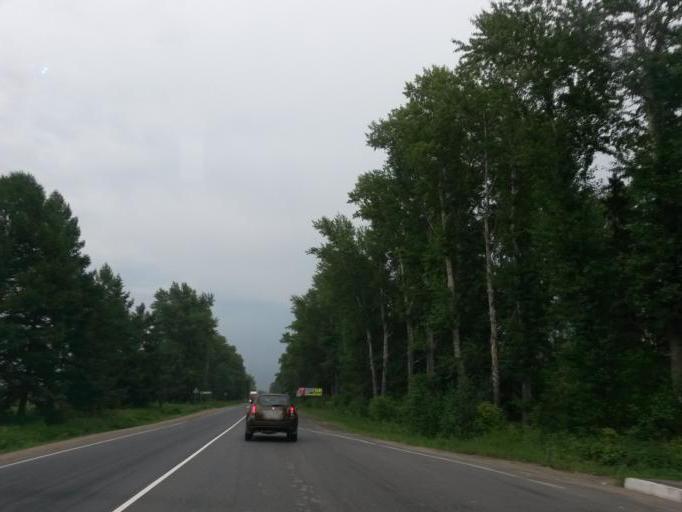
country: RU
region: Moskovskaya
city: Yam
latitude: 55.4546
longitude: 37.6764
